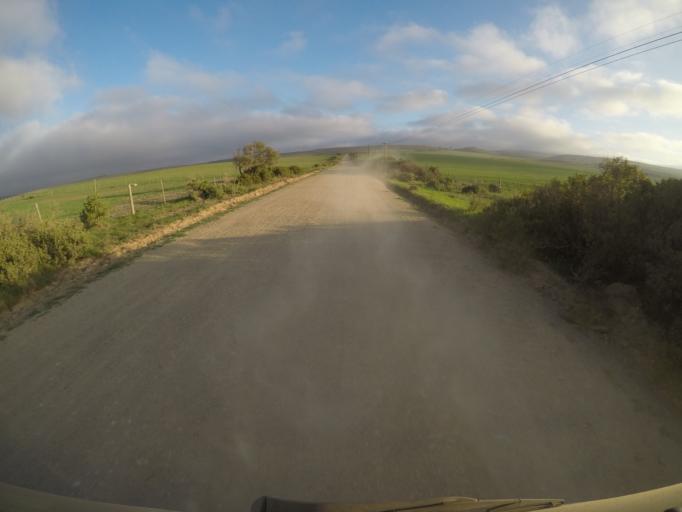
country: ZA
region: Western Cape
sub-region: Eden District Municipality
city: Mossel Bay
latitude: -34.1154
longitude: 22.0533
